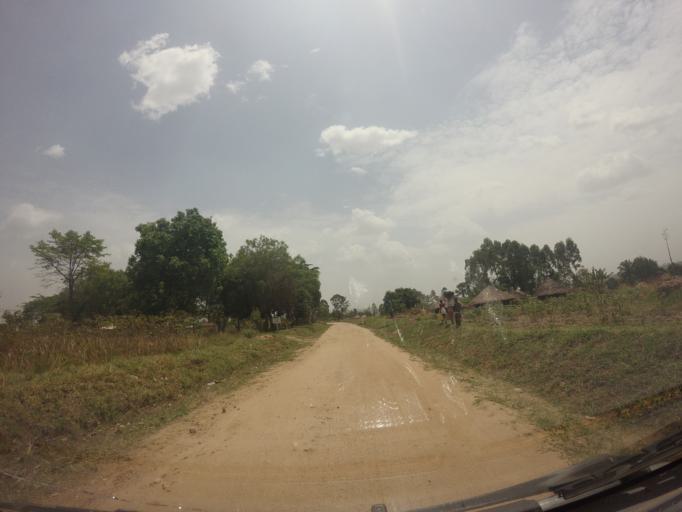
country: UG
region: Northern Region
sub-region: Arua District
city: Arua
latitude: 2.9451
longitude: 30.9131
